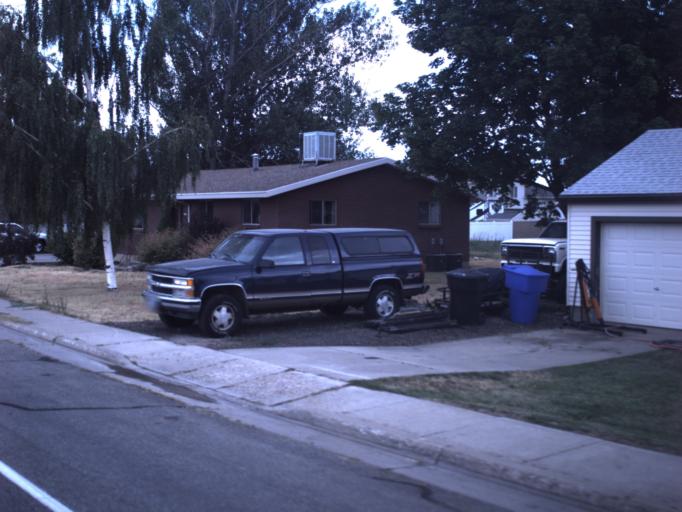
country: US
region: Utah
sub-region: Davis County
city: West Point
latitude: 41.1181
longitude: -112.0887
